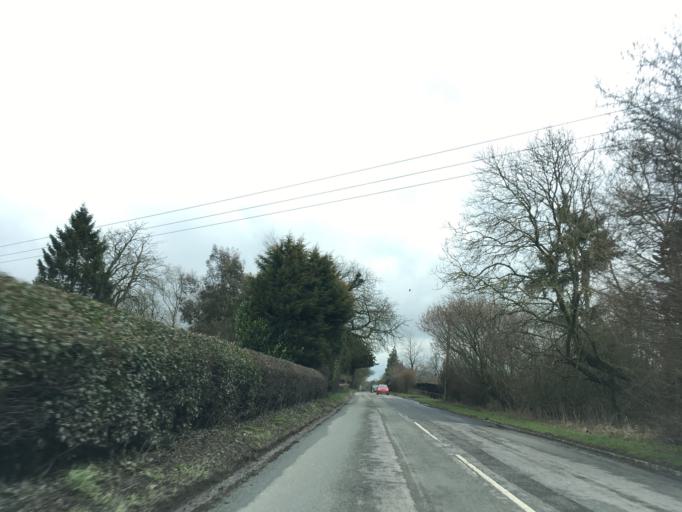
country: GB
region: England
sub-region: West Berkshire
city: Lambourn
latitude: 51.4836
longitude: -1.5495
